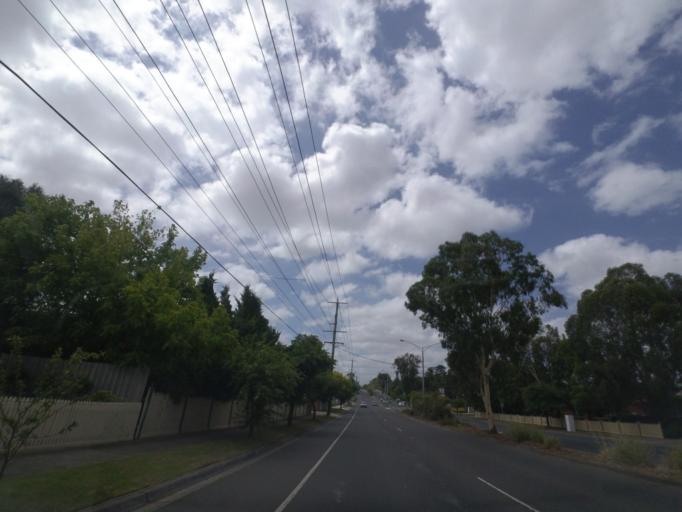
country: AU
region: Victoria
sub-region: Maroondah
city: Croydon South
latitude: -37.8049
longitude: 145.2888
